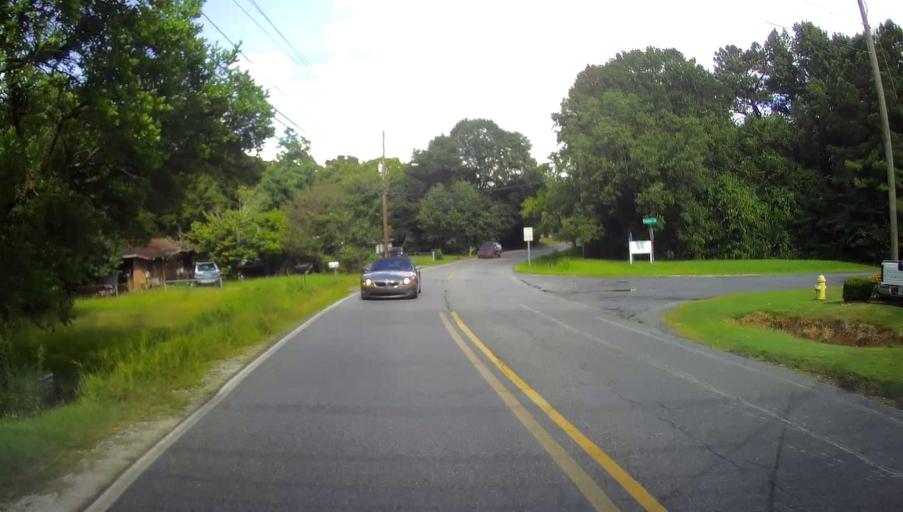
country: US
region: Alabama
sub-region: Russell County
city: Phenix City
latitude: 32.5224
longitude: -84.9724
